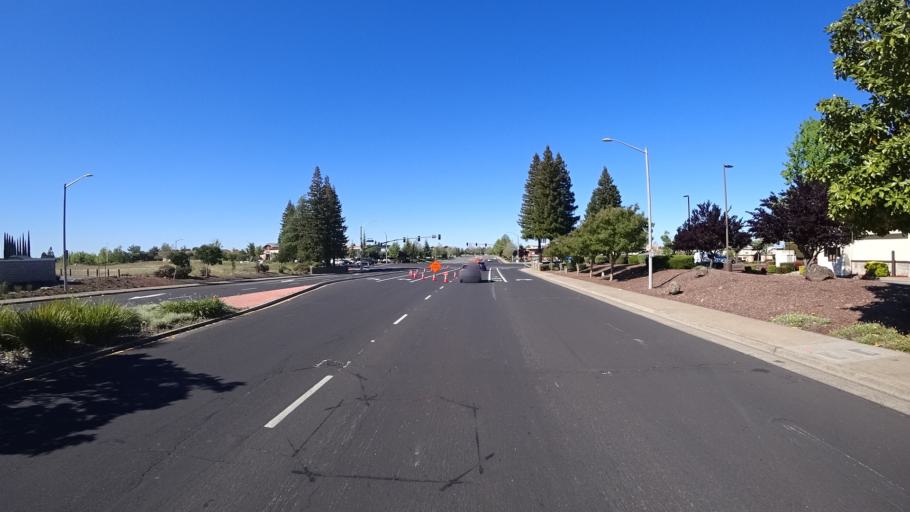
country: US
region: California
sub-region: Placer County
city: Rocklin
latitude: 38.7968
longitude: -121.2641
